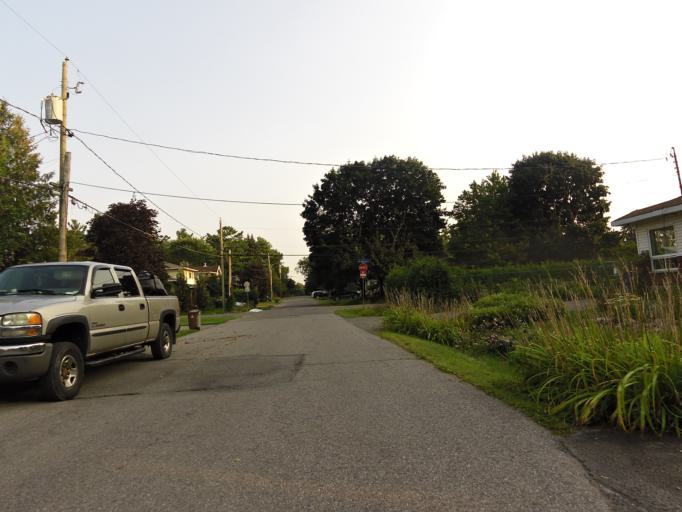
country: CA
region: Ontario
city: Bells Corners
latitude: 45.3872
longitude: -75.8443
